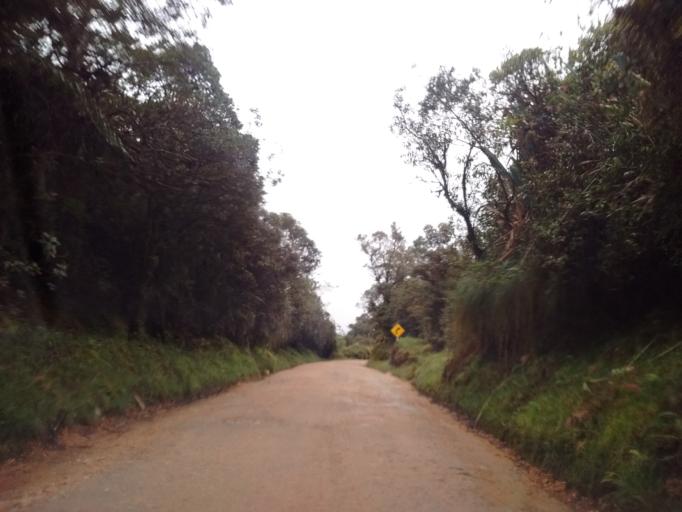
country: CO
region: Huila
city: Isnos
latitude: 2.1169
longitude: -76.3757
